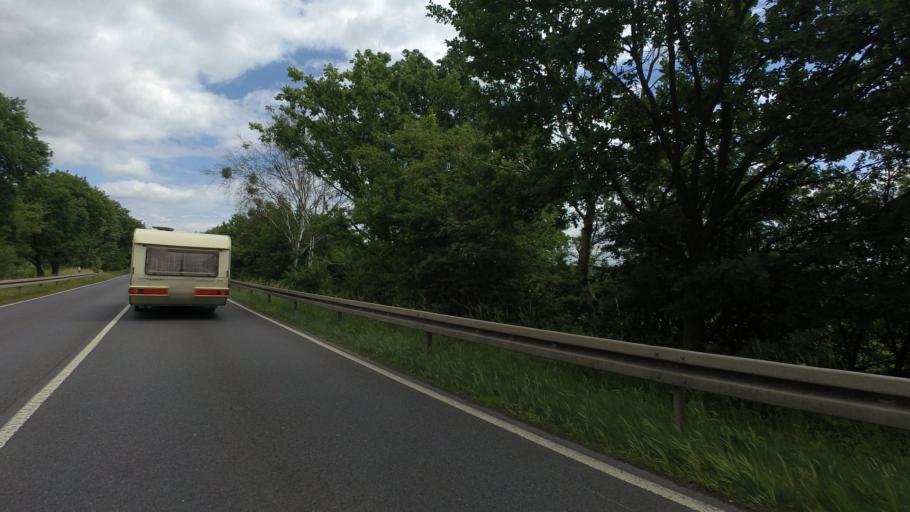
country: DE
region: Brandenburg
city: Grossraschen
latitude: 51.5872
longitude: 13.9450
